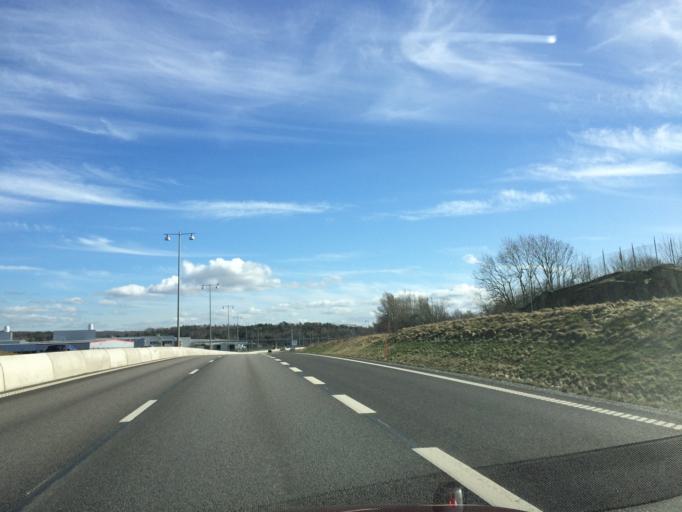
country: SE
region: Vaestra Goetaland
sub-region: Goteborg
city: Torslanda
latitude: 57.7150
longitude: 11.8315
